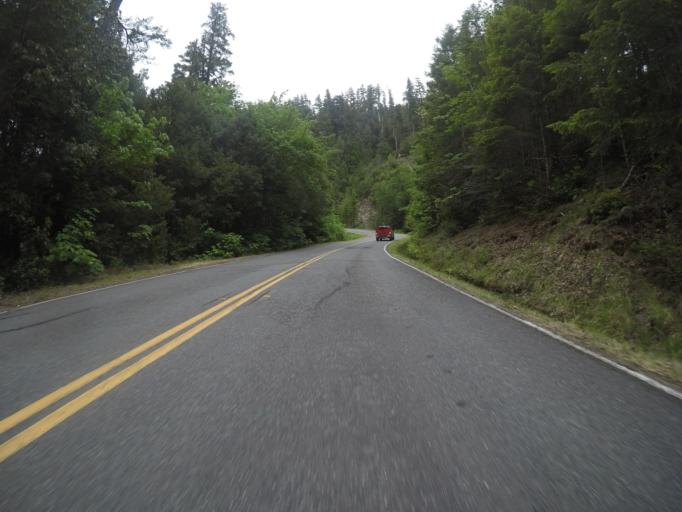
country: US
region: California
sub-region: Del Norte County
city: Bertsch-Oceanview
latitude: 41.7232
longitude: -123.9536
